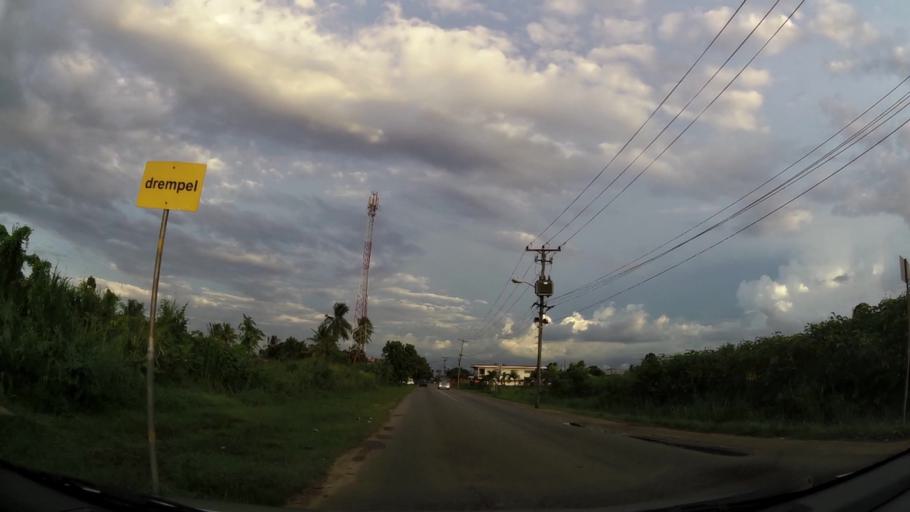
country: SR
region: Paramaribo
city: Paramaribo
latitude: 5.7761
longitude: -55.1683
